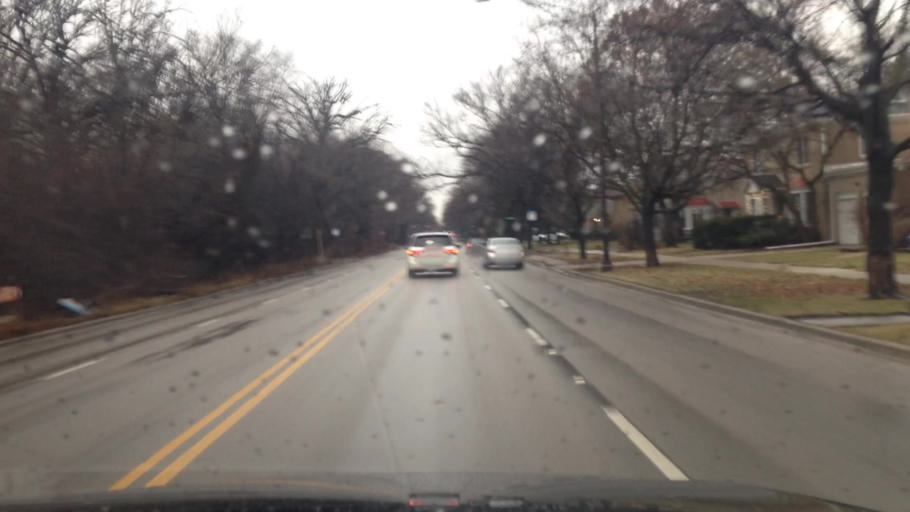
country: US
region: Illinois
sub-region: Cook County
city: Lincolnwood
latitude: 41.9931
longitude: -87.7576
